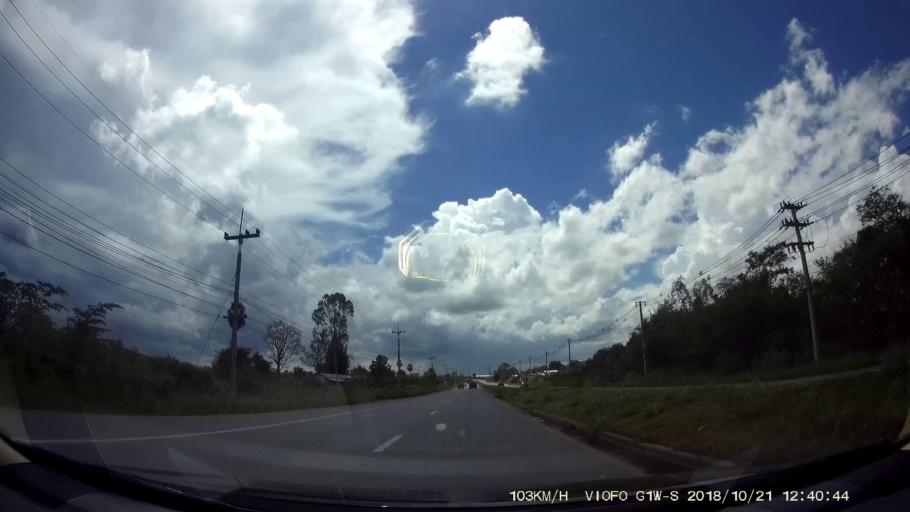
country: TH
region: Nakhon Ratchasima
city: Amphoe Sikhiu
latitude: 15.0210
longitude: 101.6916
